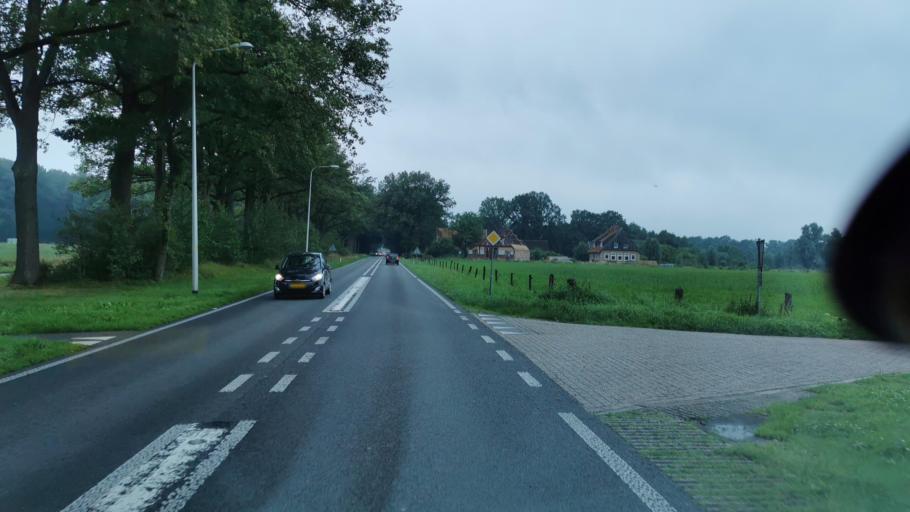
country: NL
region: Overijssel
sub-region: Gemeente Losser
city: Losser
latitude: 52.2752
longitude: 6.9784
